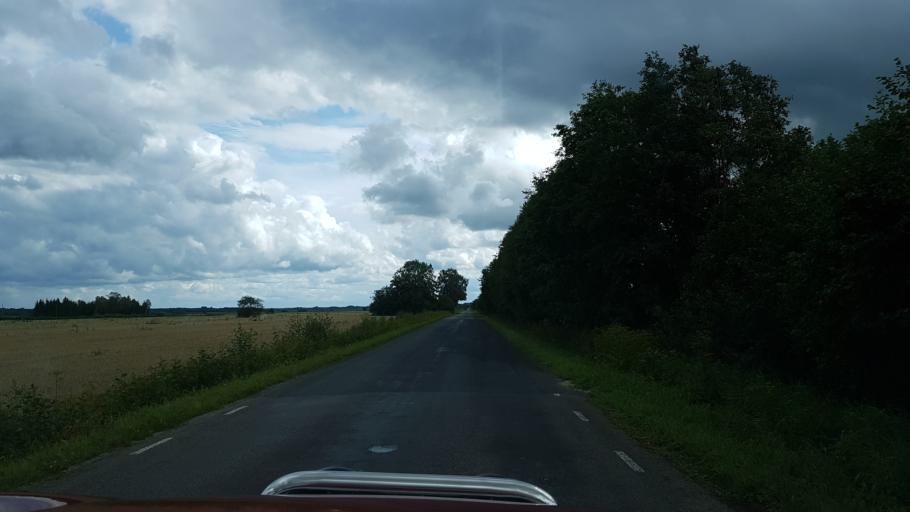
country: EE
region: Laeaene
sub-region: Lihula vald
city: Lihula
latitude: 58.7212
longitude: 23.9724
